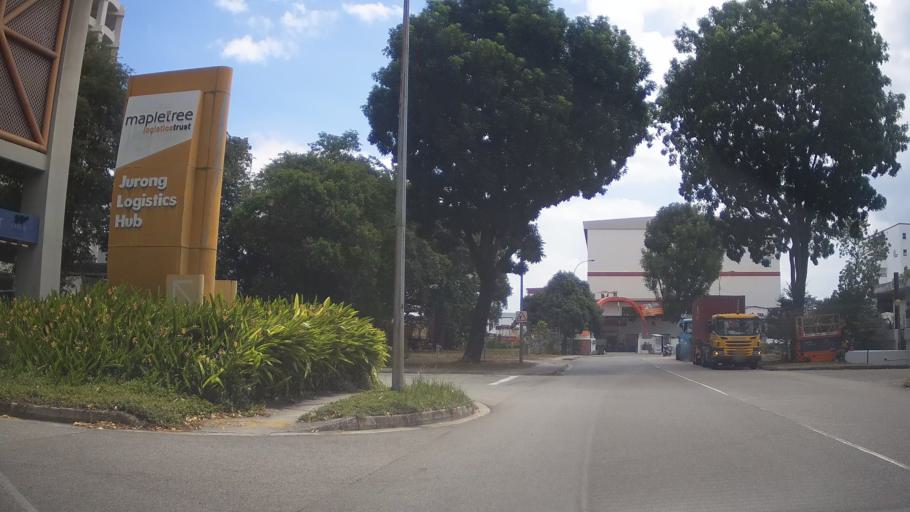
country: SG
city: Singapore
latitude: 1.3112
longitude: 103.7200
